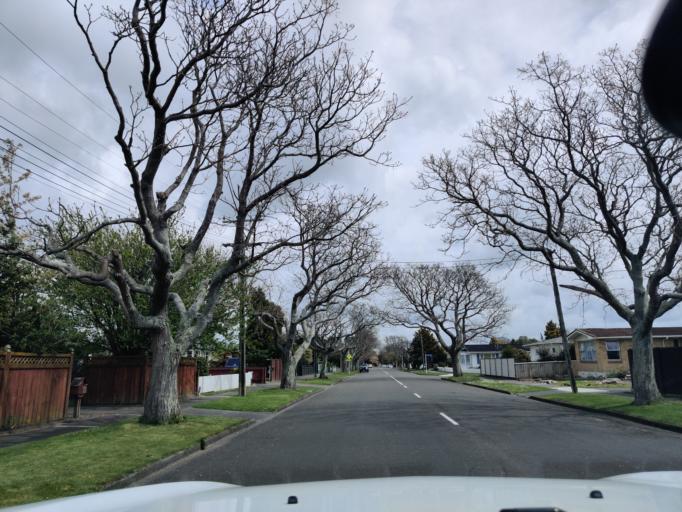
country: NZ
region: Manawatu-Wanganui
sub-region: Palmerston North City
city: Palmerston North
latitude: -40.3779
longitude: 175.5964
